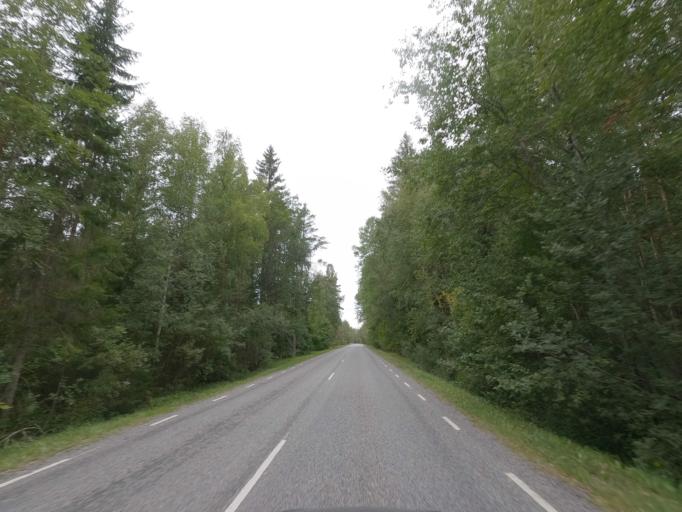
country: EE
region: Raplamaa
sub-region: Rapla vald
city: Rapla
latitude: 59.0083
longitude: 24.6107
